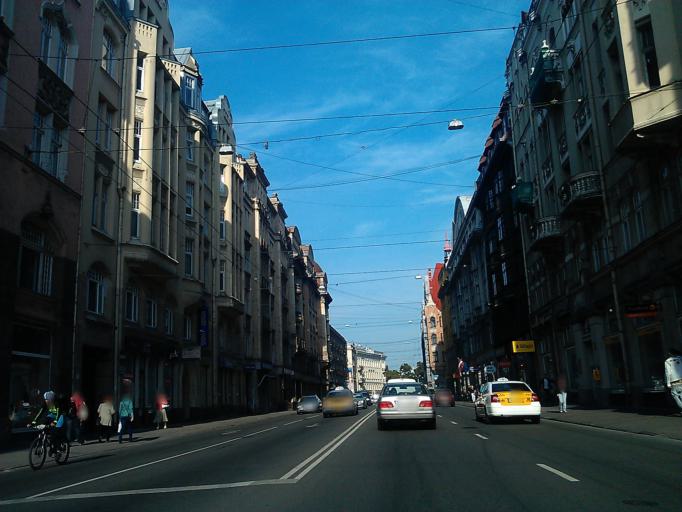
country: LV
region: Riga
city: Riga
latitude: 56.9573
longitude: 24.1230
